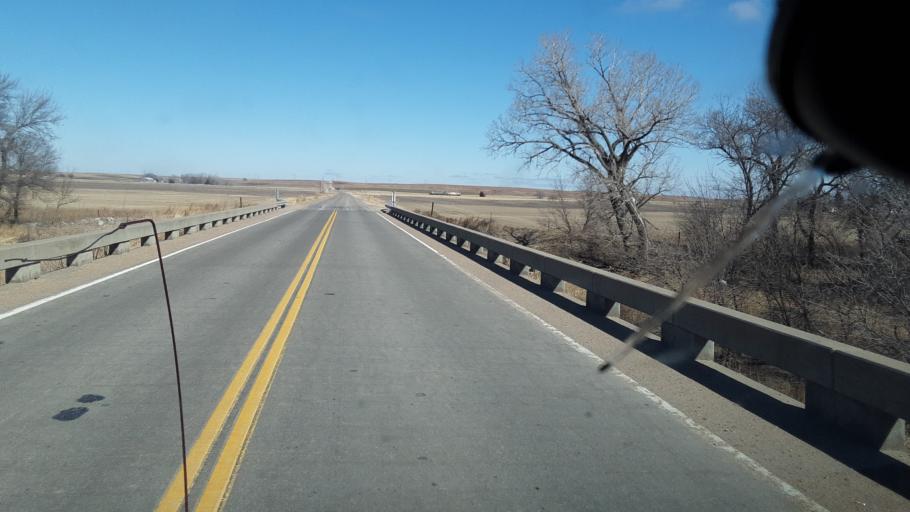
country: US
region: Kansas
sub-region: Barton County
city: Ellinwood
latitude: 38.3567
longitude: -98.6641
